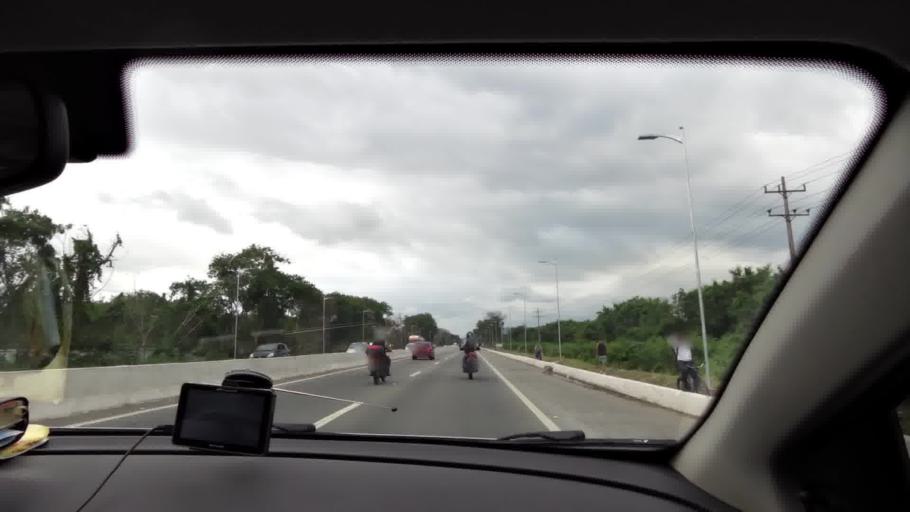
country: BR
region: Espirito Santo
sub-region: Vila Velha
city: Vila Velha
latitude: -20.2446
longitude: -40.2826
